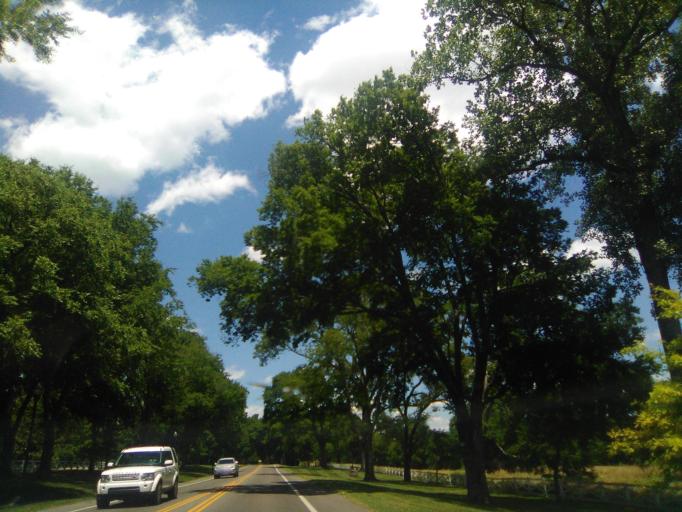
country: US
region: Tennessee
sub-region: Davidson County
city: Belle Meade
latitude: 36.1170
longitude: -86.8611
